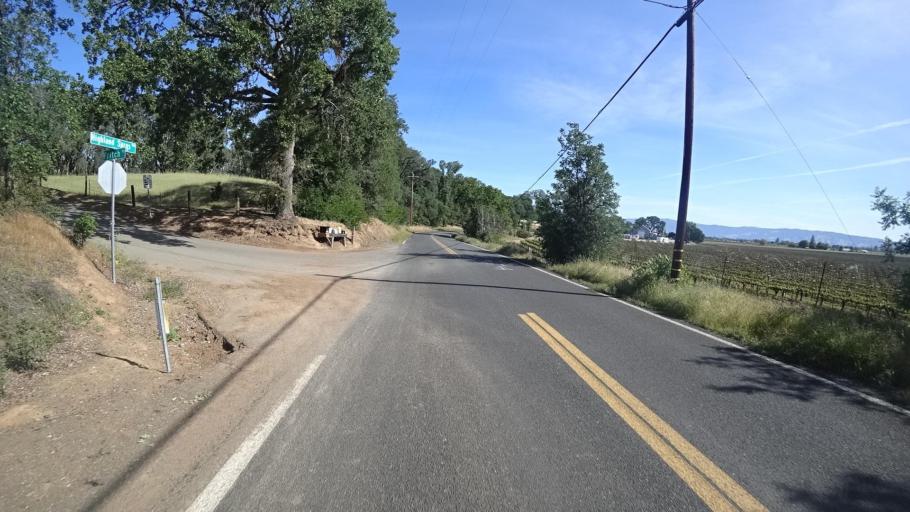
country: US
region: California
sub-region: Lake County
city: Kelseyville
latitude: 38.9684
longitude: -122.8978
